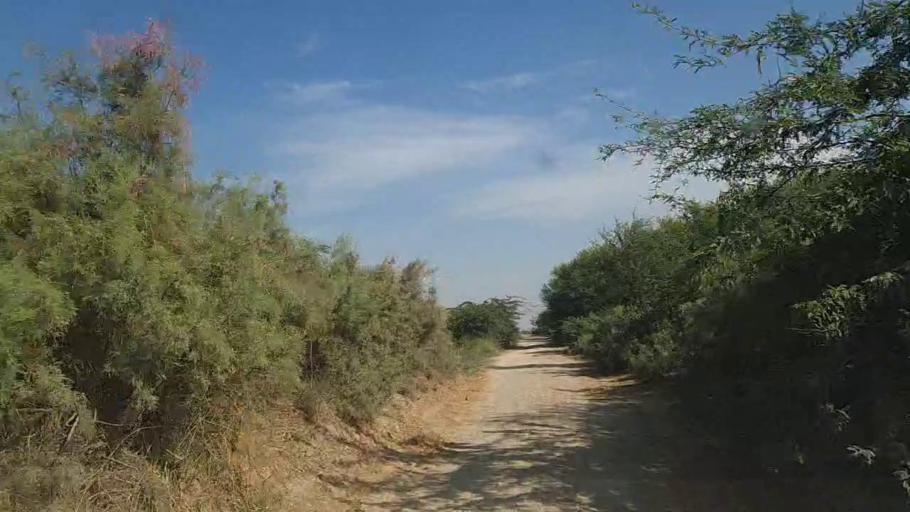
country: PK
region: Sindh
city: Bulri
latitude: 24.8643
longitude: 68.2656
